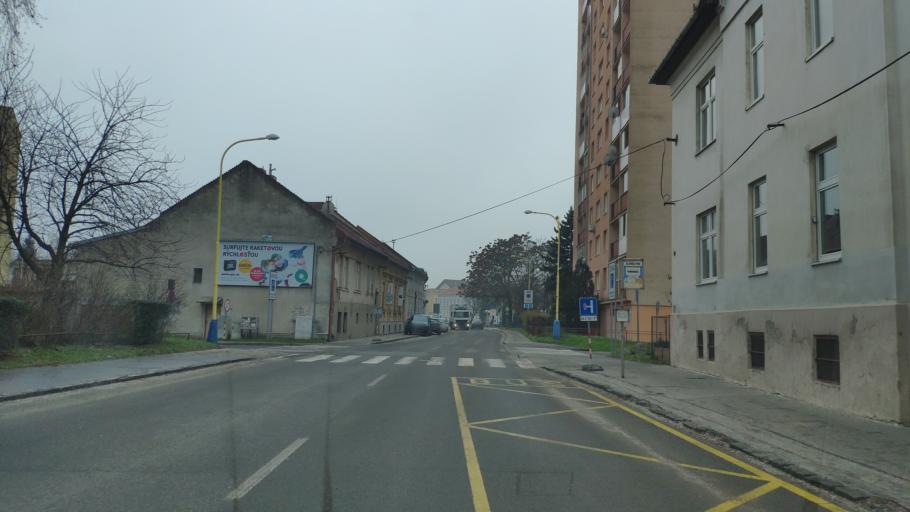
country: SK
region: Kosicky
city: Kosice
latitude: 48.7307
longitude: 21.2609
